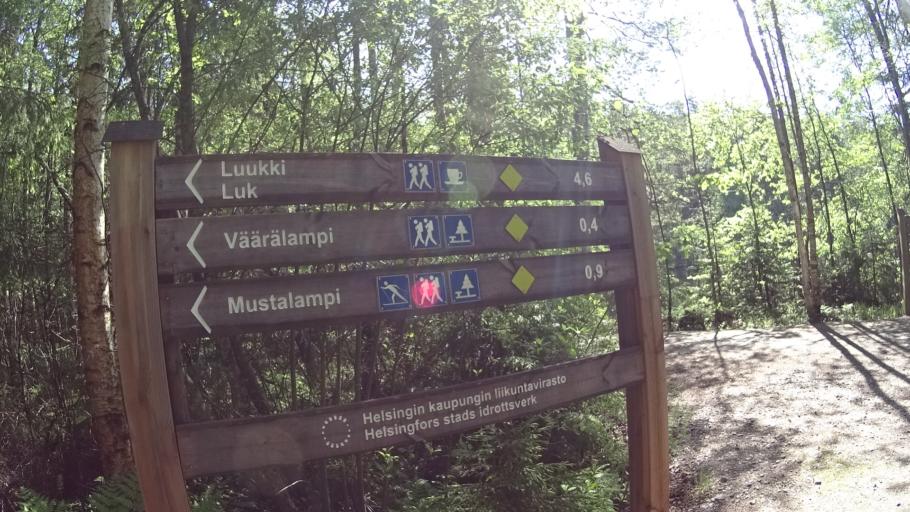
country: FI
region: Uusimaa
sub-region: Helsinki
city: Espoo
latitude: 60.3332
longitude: 24.6685
